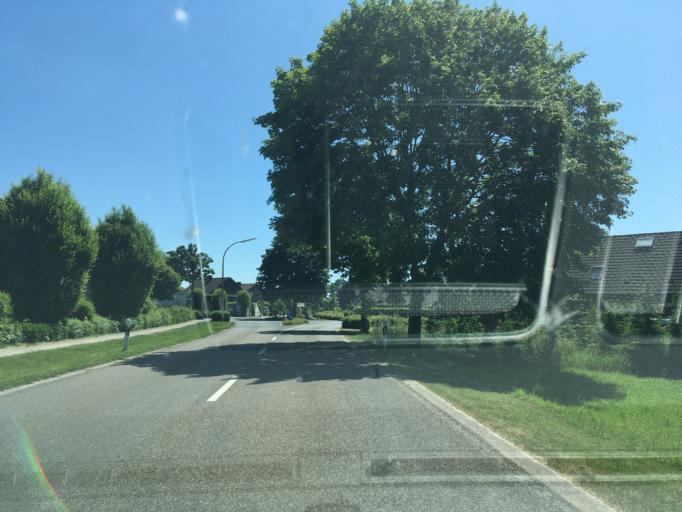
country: DE
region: North Rhine-Westphalia
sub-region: Regierungsbezirk Munster
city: Raesfeld
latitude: 51.7745
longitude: 6.8315
